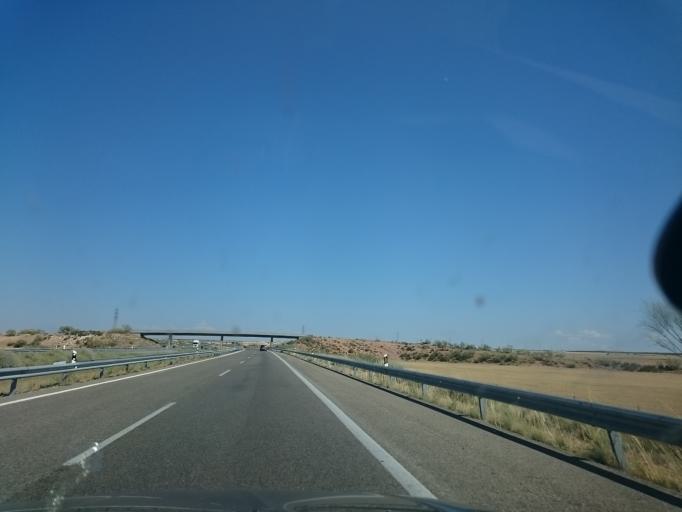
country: ES
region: Aragon
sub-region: Provincia de Zaragoza
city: Mequinensa / Mequinenza
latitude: 41.4713
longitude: 0.2180
